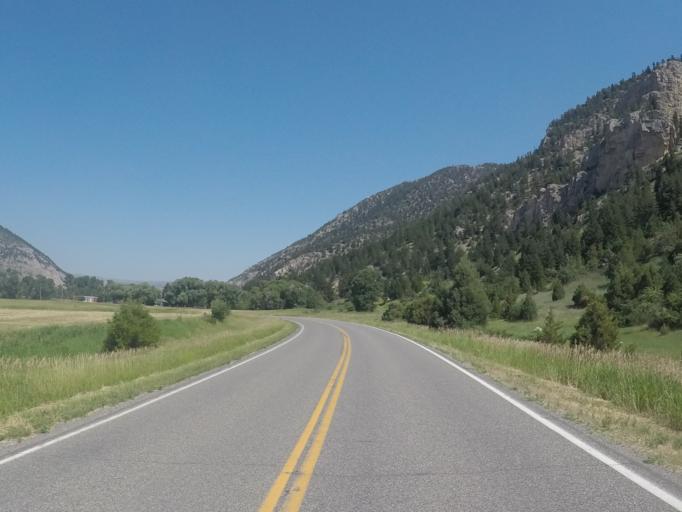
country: US
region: Montana
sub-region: Park County
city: Livingston
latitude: 45.5930
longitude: -110.5613
